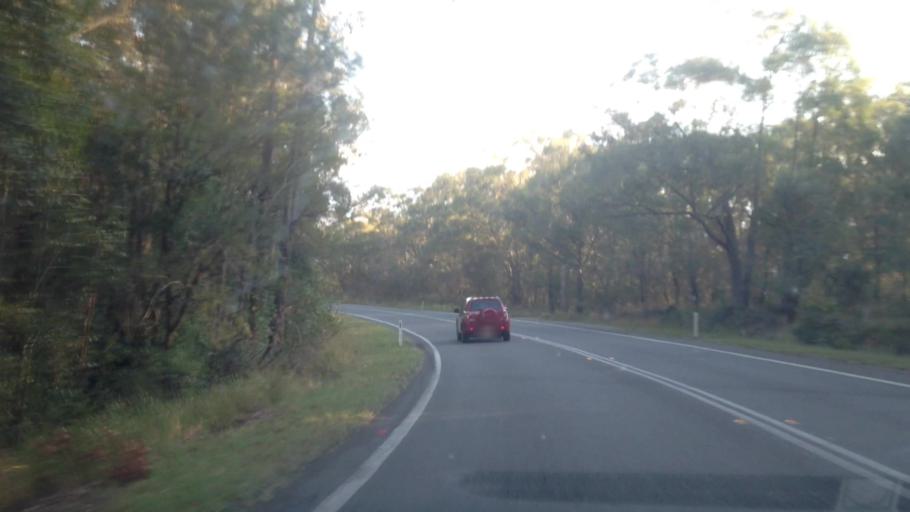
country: AU
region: New South Wales
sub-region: Lake Macquarie Shire
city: Dora Creek
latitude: -33.0036
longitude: 151.4892
